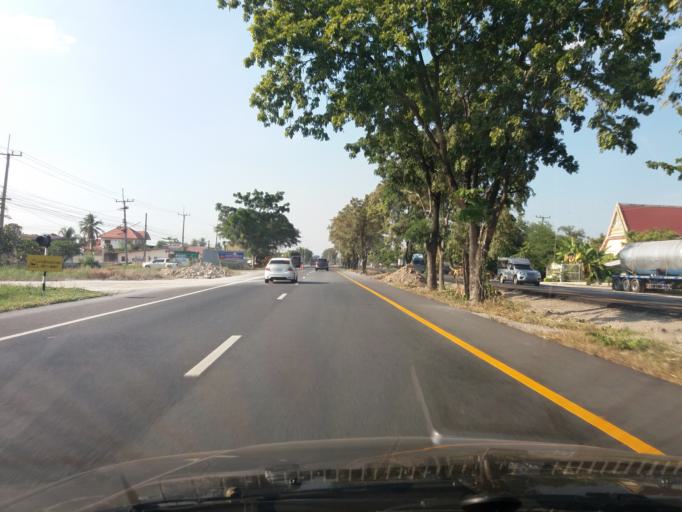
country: TH
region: Nakhon Sawan
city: Banphot Phisai
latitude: 15.8202
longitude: 99.9405
